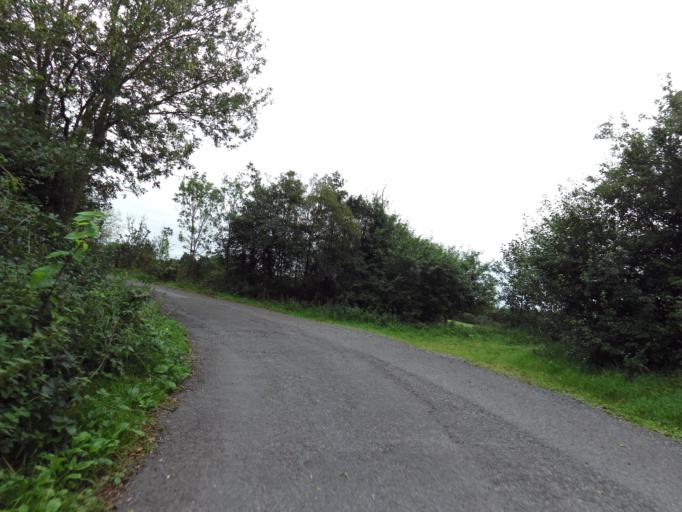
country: IE
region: Leinster
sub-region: Uibh Fhaili
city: Ferbane
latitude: 53.2432
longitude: -7.7437
